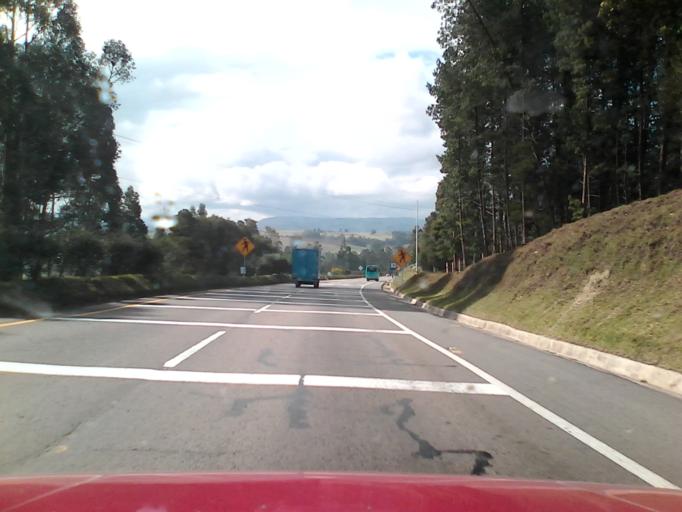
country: CO
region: Boyaca
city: Tuta
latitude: 5.6718
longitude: -73.2696
